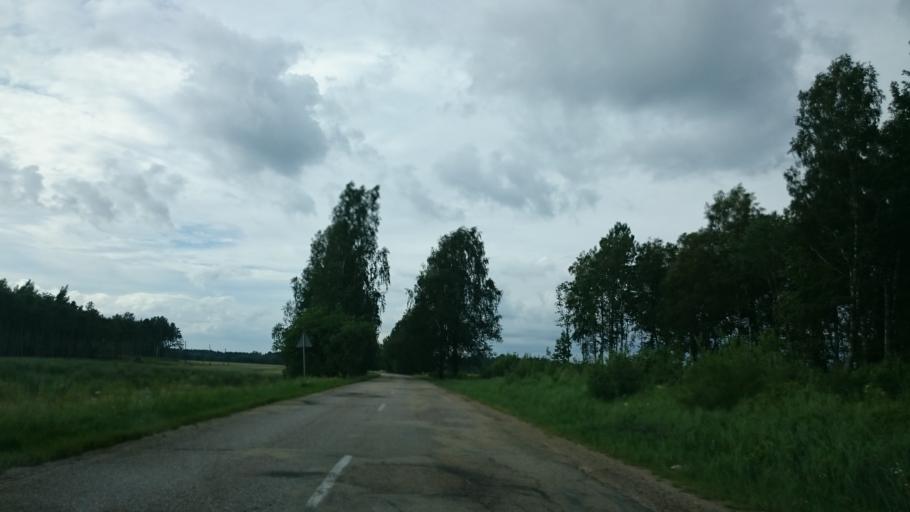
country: LV
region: Saulkrastu
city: Saulkrasti
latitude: 57.2431
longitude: 24.5217
